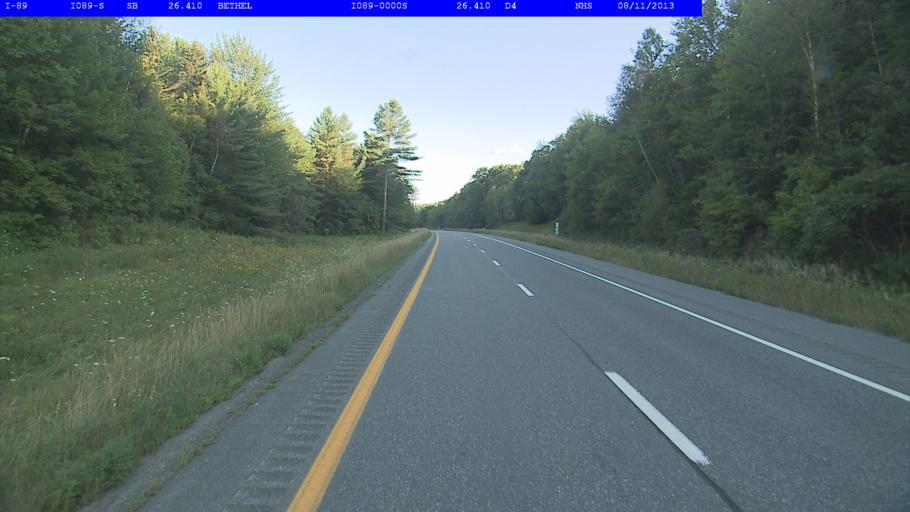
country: US
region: Vermont
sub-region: Orange County
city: Randolph
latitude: 43.8810
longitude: -72.6168
